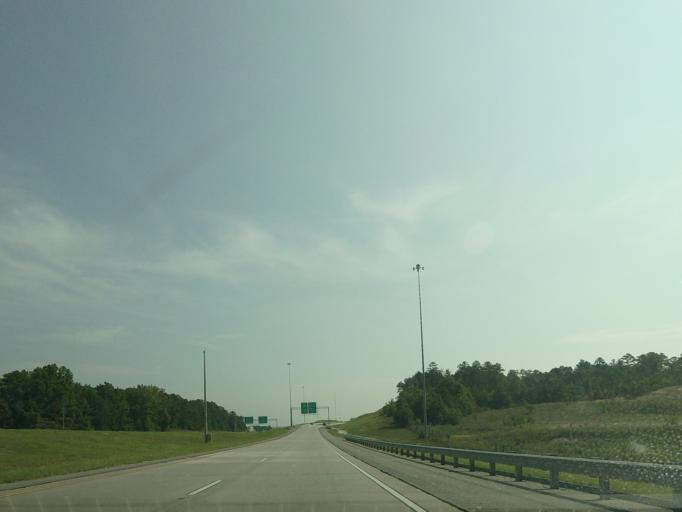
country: US
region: Georgia
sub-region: Bibb County
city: West Point
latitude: 32.7503
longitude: -83.7135
